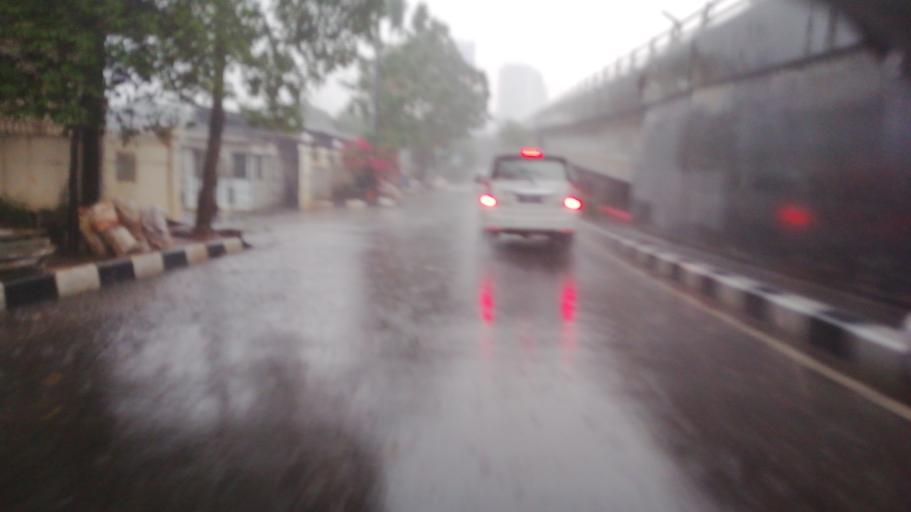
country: ID
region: Jakarta Raya
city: Jakarta
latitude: -6.3037
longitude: 106.8415
